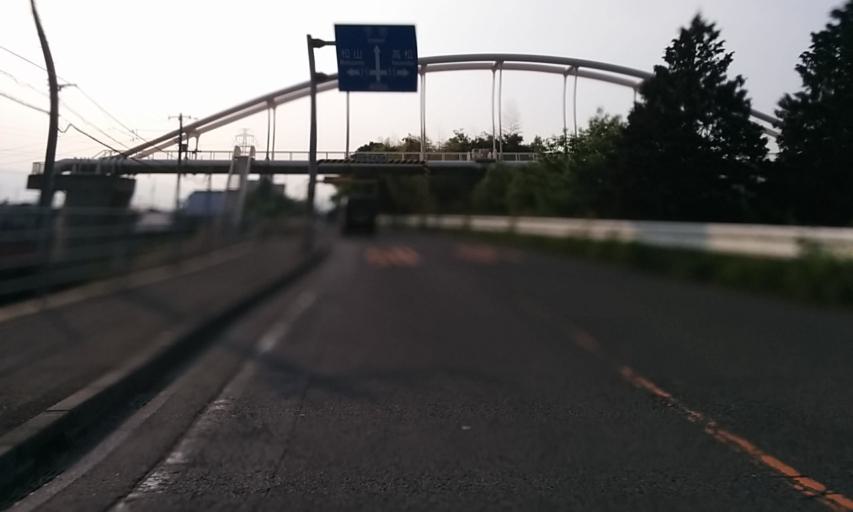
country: JP
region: Ehime
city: Saijo
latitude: 33.9004
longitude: 133.1875
